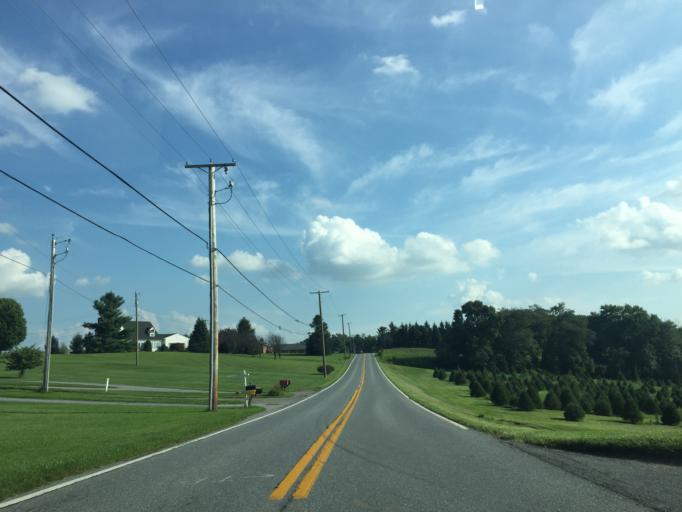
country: US
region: Maryland
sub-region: Carroll County
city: Hampstead
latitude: 39.6277
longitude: -76.7945
